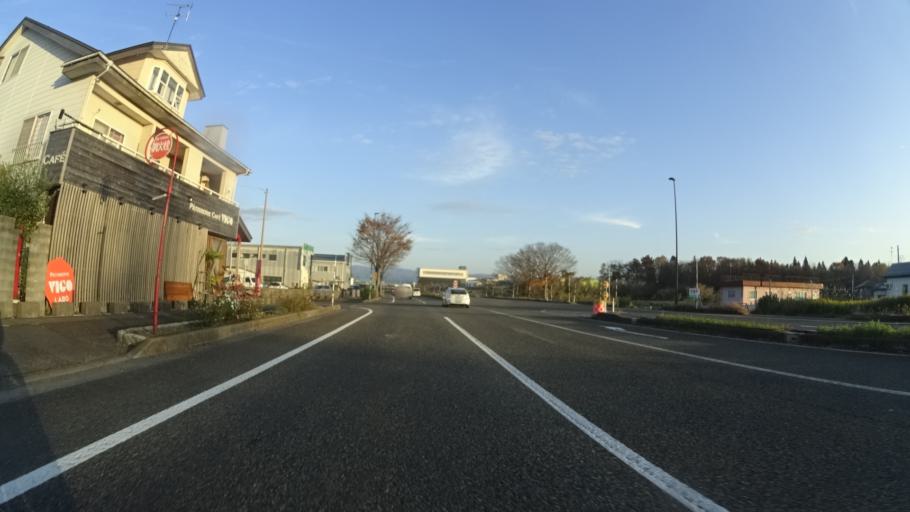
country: JP
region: Niigata
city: Nagaoka
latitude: 37.4457
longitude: 138.7770
